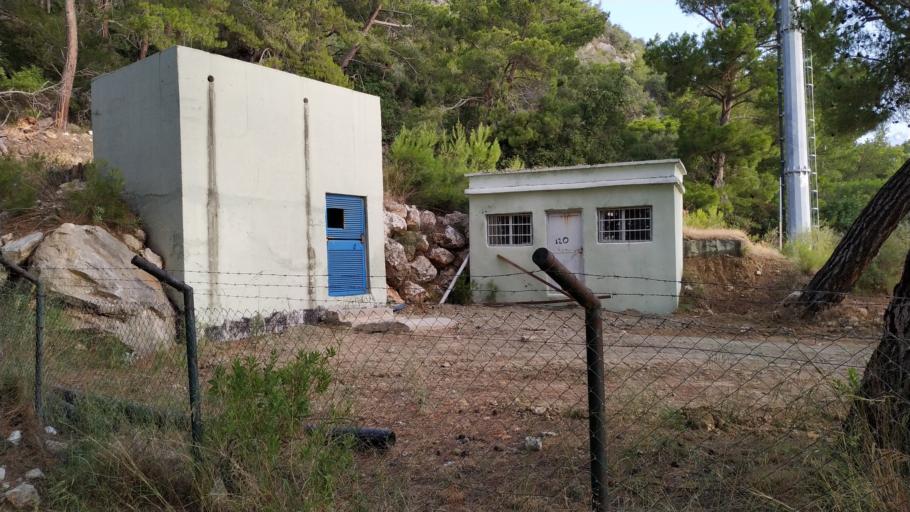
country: TR
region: Antalya
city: Tekirova
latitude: 36.4121
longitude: 30.4775
